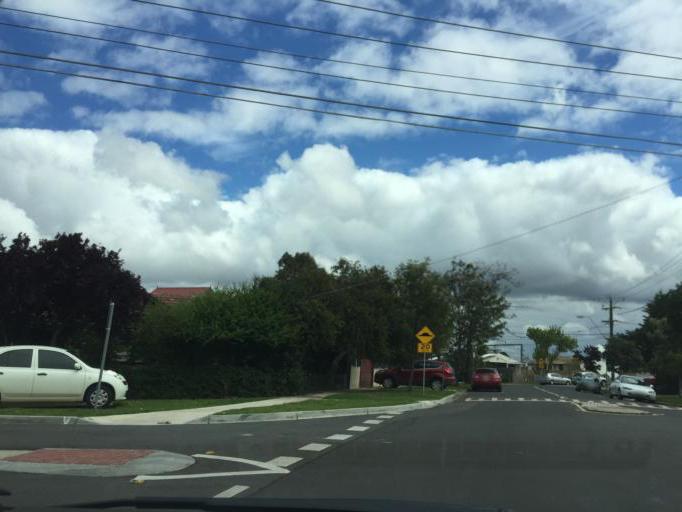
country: AU
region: Victoria
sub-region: Maribyrnong
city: Braybrook
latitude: -37.7911
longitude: 144.8369
